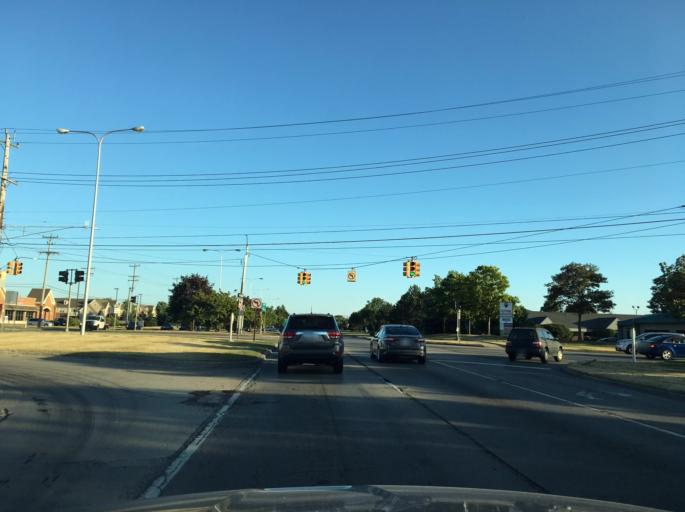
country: US
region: Michigan
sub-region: Macomb County
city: Utica
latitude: 42.6155
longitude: -82.9926
